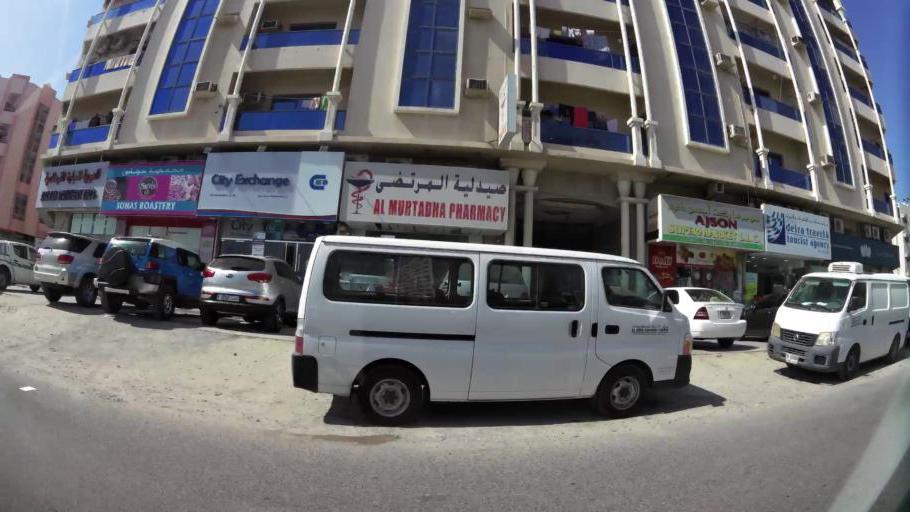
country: AE
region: Ajman
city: Ajman
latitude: 25.4100
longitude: 55.4441
